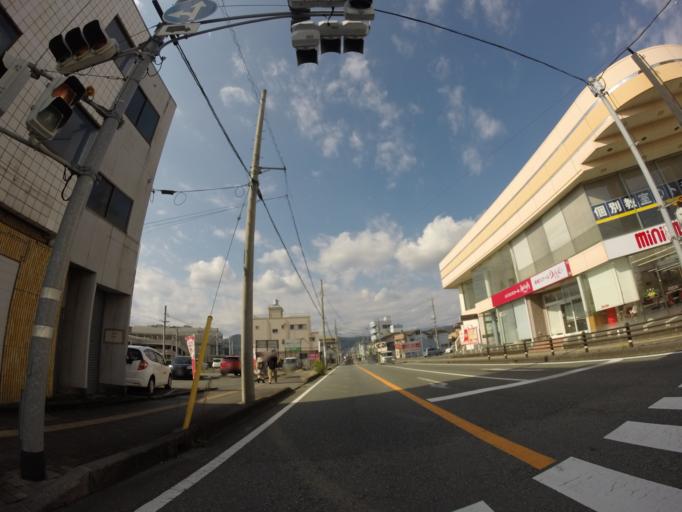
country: JP
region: Shizuoka
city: Fujinomiya
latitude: 35.2220
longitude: 138.6136
